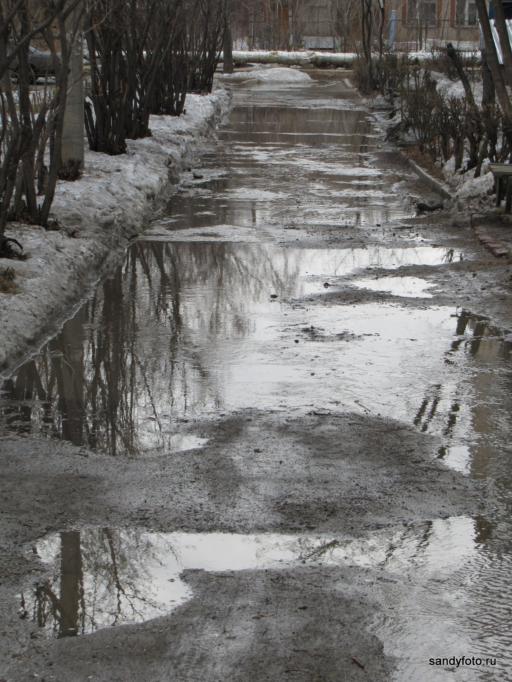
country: RU
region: Chelyabinsk
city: Troitsk
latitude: 54.1052
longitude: 61.5582
